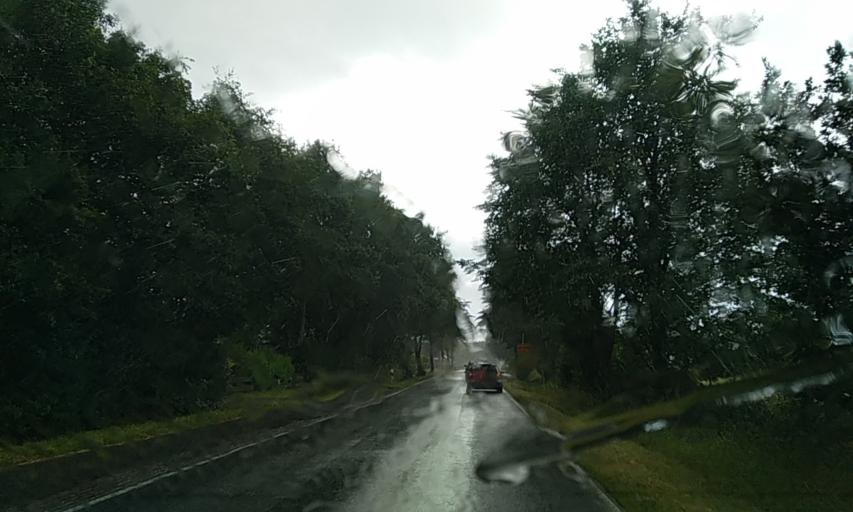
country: DE
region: Schleswig-Holstein
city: Lurschau
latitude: 54.5446
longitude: 9.4953
